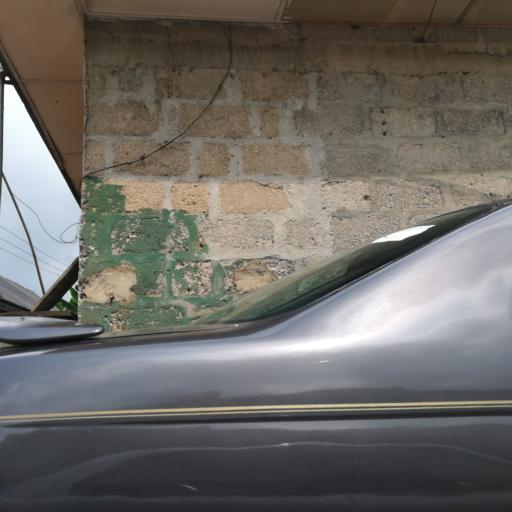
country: NG
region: Rivers
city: Port Harcourt
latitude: 4.8363
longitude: 7.0764
